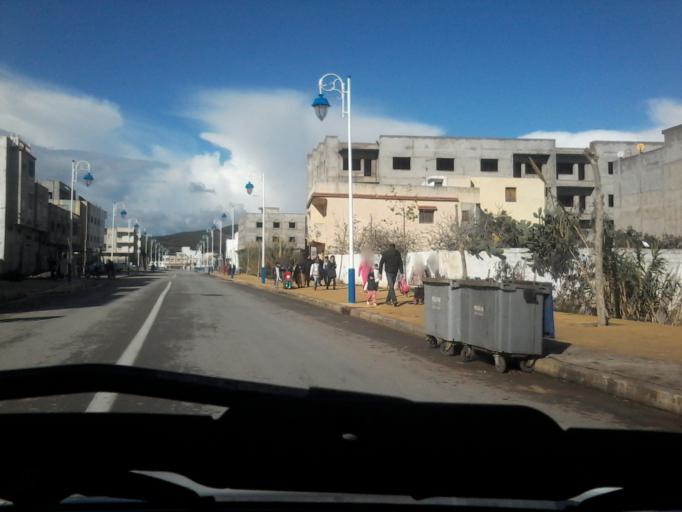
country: MA
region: Tanger-Tetouan
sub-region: Tetouan
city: Martil
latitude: 35.6998
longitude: -5.3489
